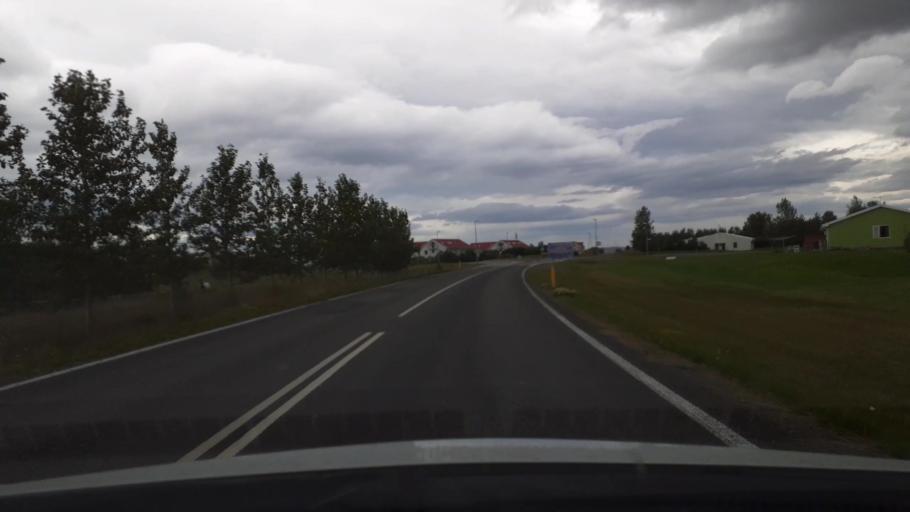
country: IS
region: West
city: Borgarnes
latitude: 64.5601
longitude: -21.7596
